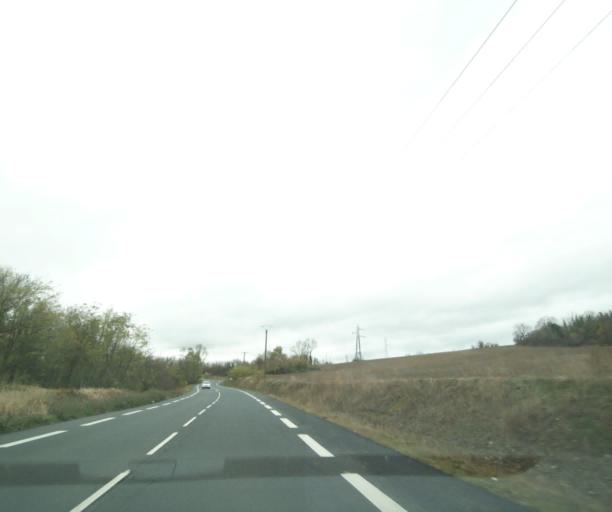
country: FR
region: Auvergne
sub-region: Departement du Puy-de-Dome
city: Dallet
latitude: 45.7775
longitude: 3.2358
